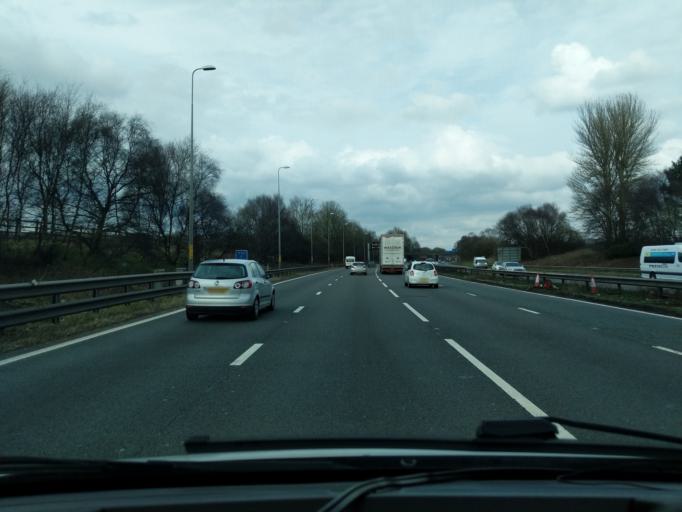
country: GB
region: England
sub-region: City and Borough of Salford
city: Walkden
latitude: 53.4762
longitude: -2.3992
